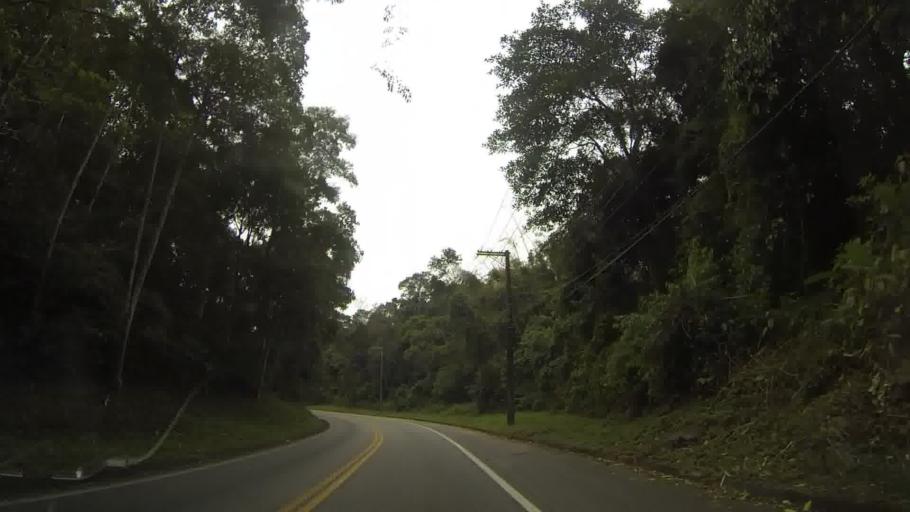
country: BR
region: Sao Paulo
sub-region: Sao Sebastiao
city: Sao Sebastiao
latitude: -23.8168
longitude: -45.4712
